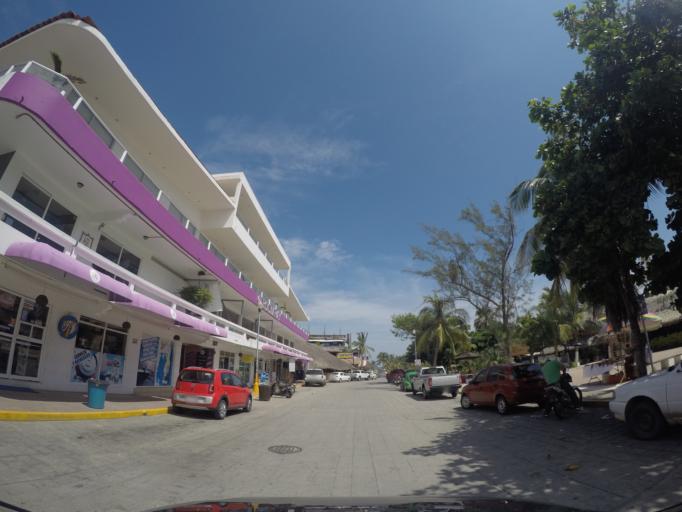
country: MX
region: Oaxaca
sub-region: Santa Maria Colotepec
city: Brisas de Zicatela
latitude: 15.8526
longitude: -97.0553
